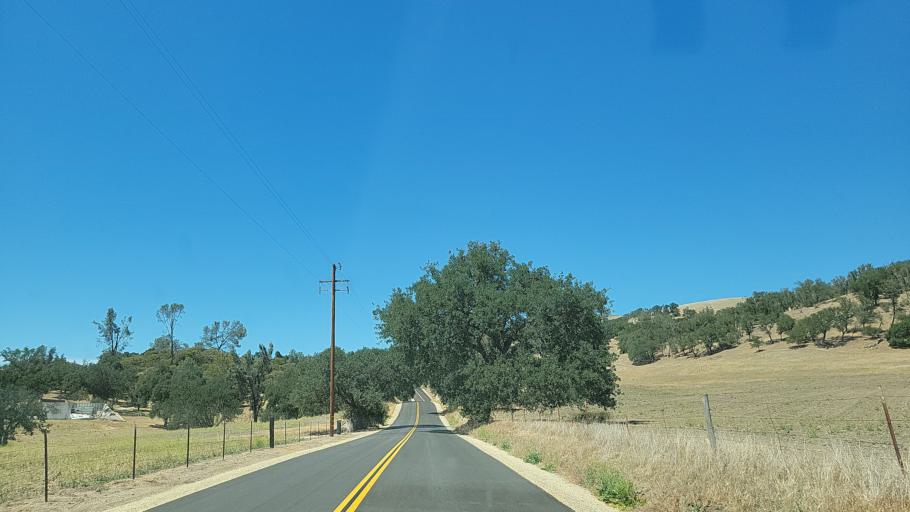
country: US
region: California
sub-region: San Luis Obispo County
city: Atascadero
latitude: 35.4724
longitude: -120.6235
